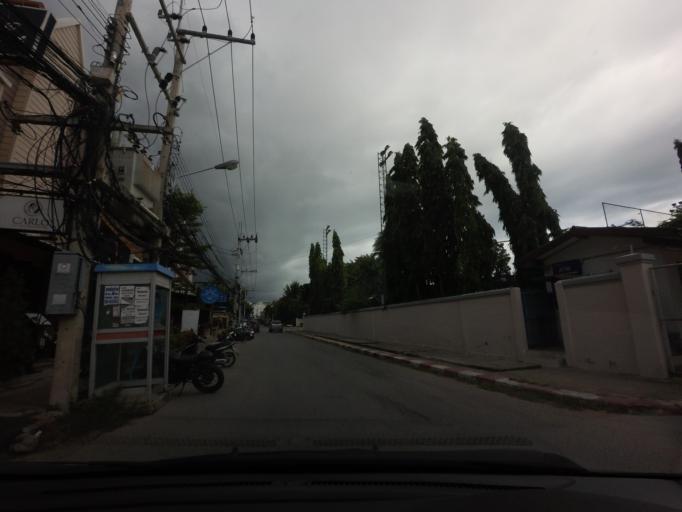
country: TH
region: Prachuap Khiri Khan
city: Hua Hin
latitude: 12.5670
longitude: 99.9601
